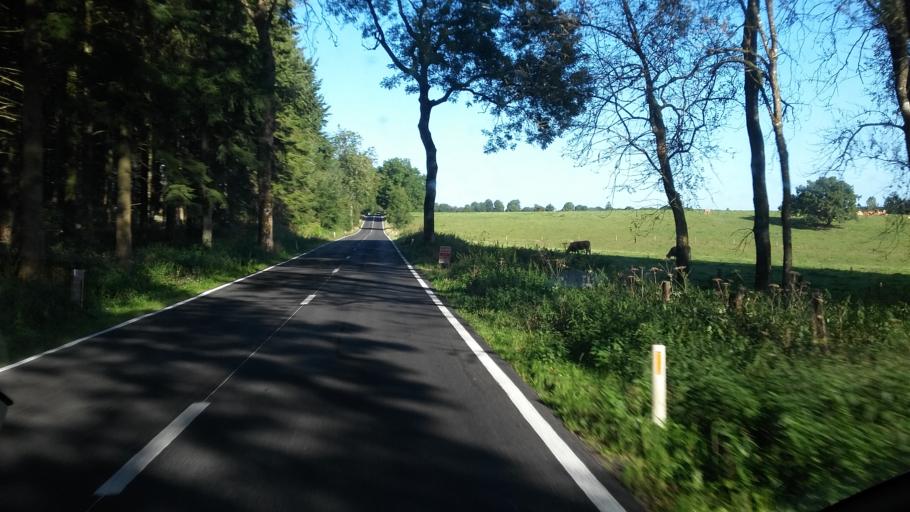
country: BE
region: Wallonia
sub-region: Province du Luxembourg
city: Leglise
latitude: 49.8167
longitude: 5.4994
